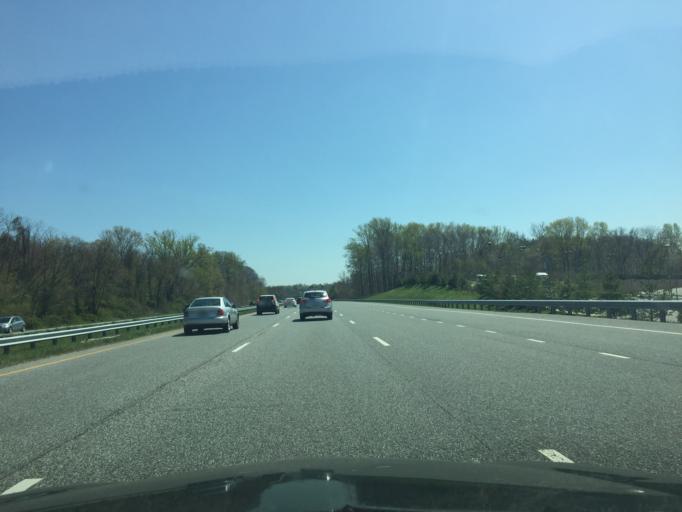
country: US
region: Maryland
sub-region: Harford County
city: South Bel Air
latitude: 39.5170
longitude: -76.3434
